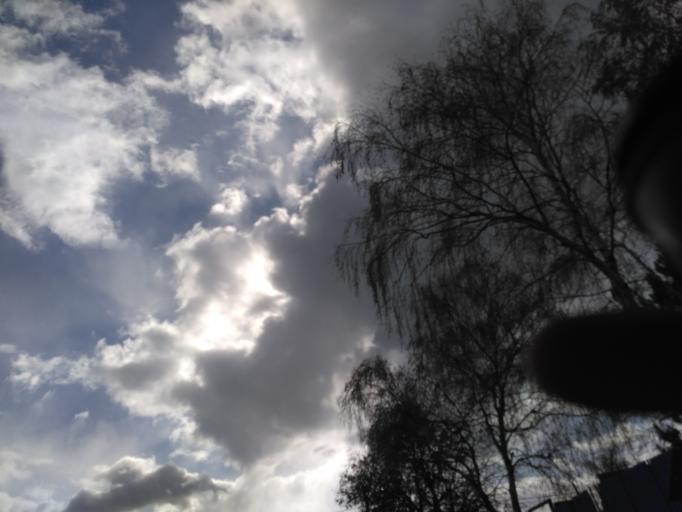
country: SK
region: Kosicky
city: Secovce
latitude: 48.6882
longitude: 21.6543
